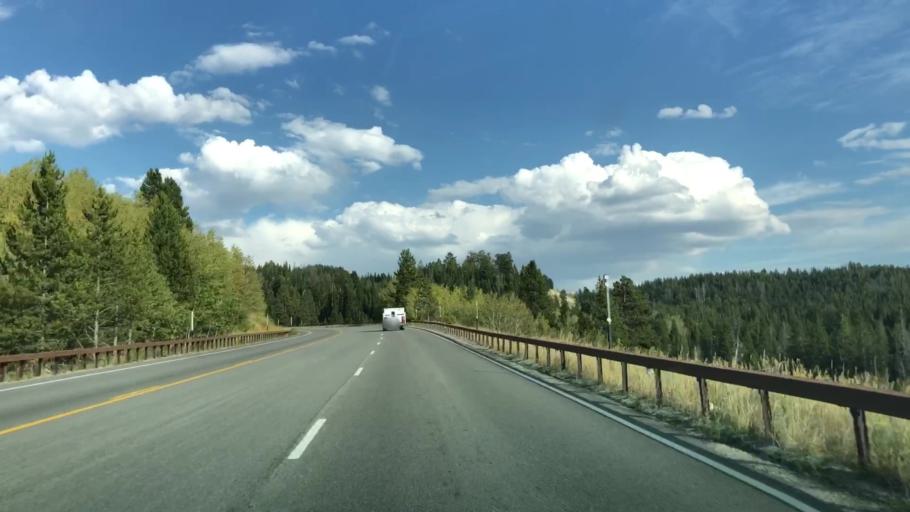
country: US
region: Wyoming
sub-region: Sublette County
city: Pinedale
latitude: 43.1388
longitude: -110.2163
